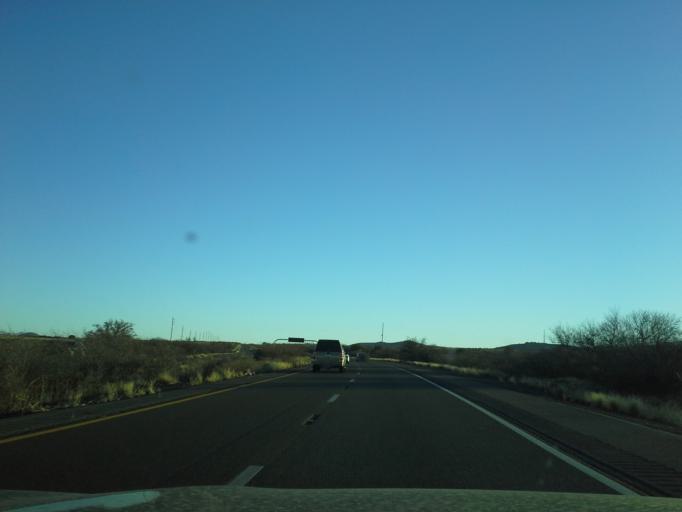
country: US
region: Arizona
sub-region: Yavapai County
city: Spring Valley
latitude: 34.3622
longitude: -112.1170
